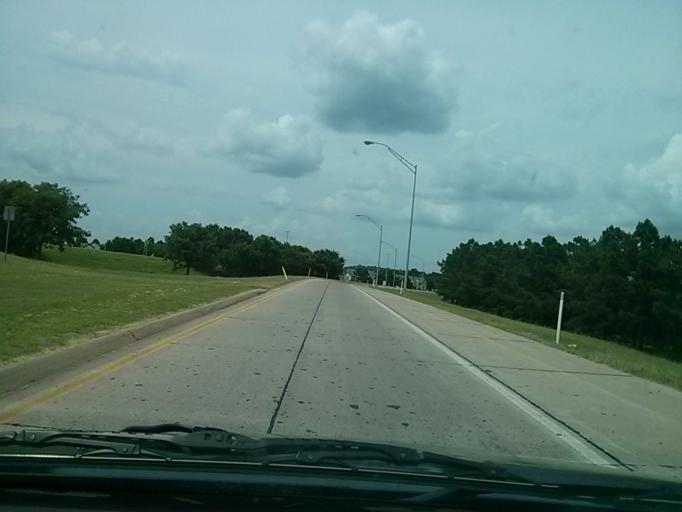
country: US
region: Oklahoma
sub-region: Tulsa County
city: Jenks
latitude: 36.0193
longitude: -95.9452
